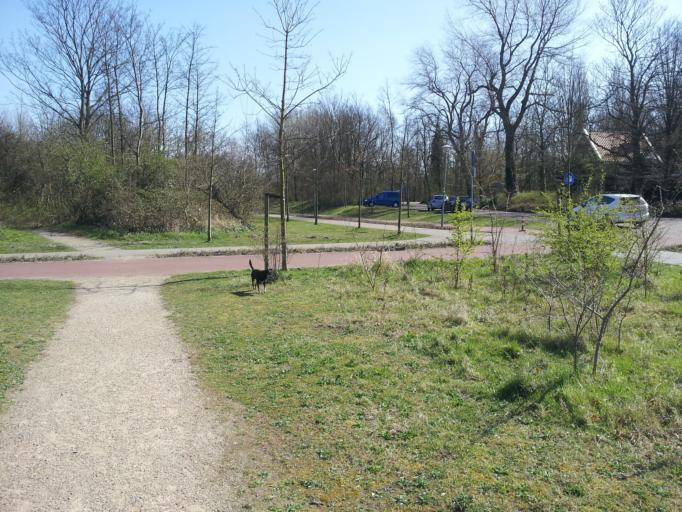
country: NL
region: South Holland
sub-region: Gemeente Rotterdam
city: Hoek van Holland
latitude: 51.9825
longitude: 4.1255
